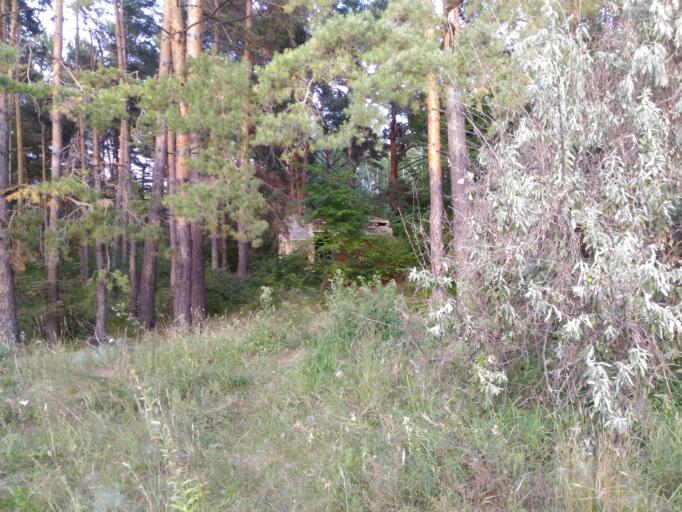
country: RU
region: Ulyanovsk
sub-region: Ulyanovskiy Rayon
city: Ulyanovsk
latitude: 54.3583
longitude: 48.5140
